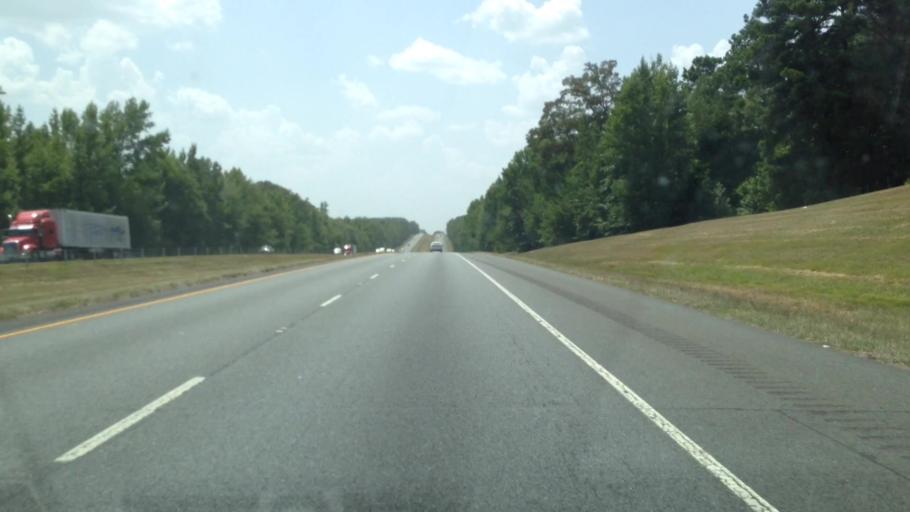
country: US
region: Louisiana
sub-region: Lincoln Parish
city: Grambling
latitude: 32.5429
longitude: -92.7249
